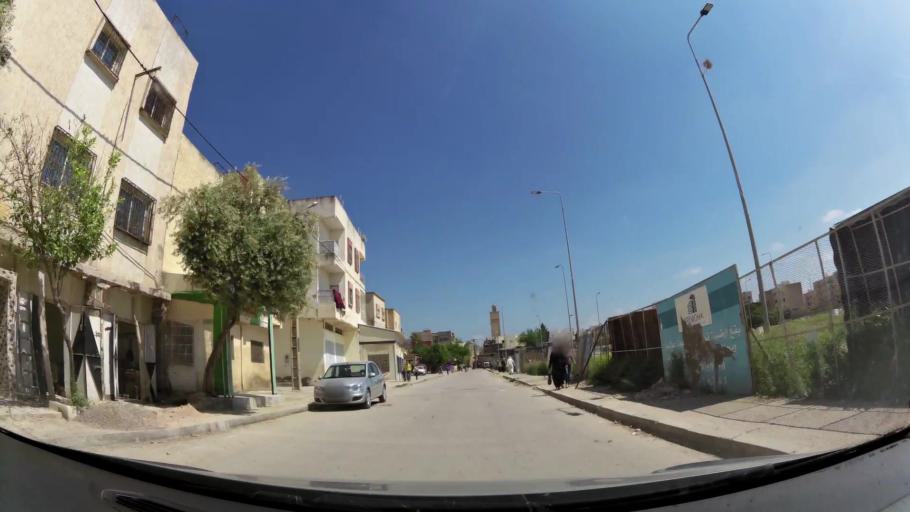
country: MA
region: Fes-Boulemane
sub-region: Fes
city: Fes
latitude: 34.0147
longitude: -5.0312
